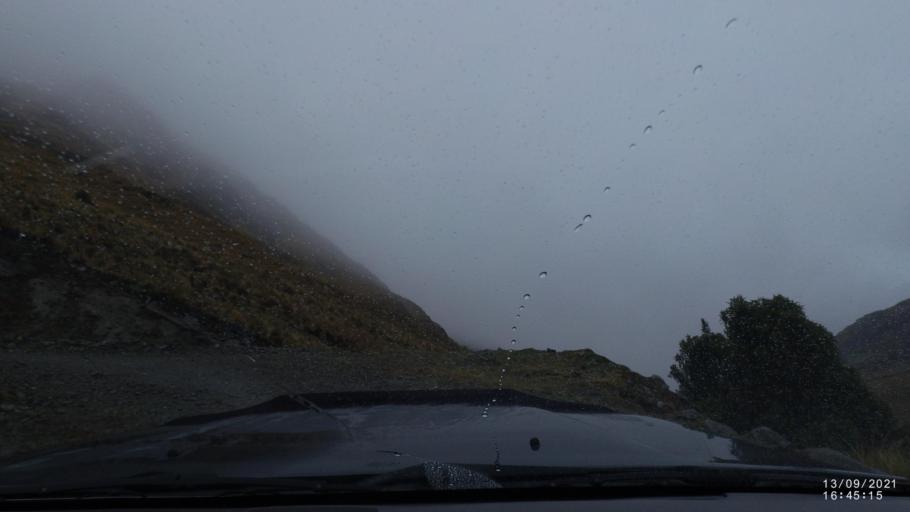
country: BO
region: Cochabamba
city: Colomi
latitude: -17.2934
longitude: -65.7114
